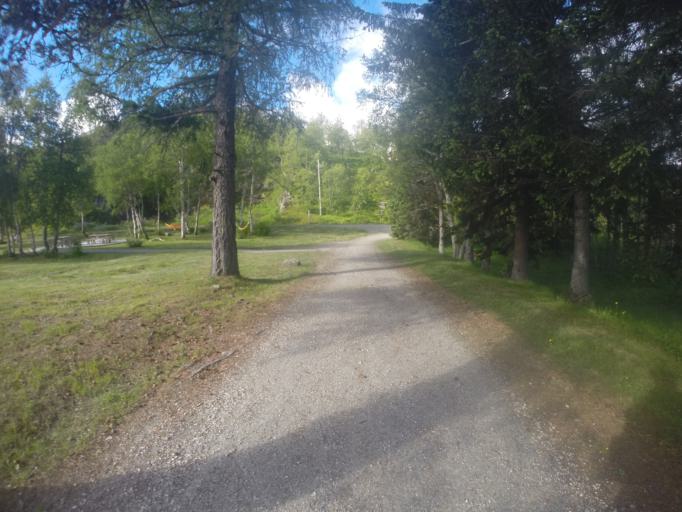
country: NO
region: Sogn og Fjordane
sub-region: Aurland
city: Aurlandsvangen
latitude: 60.7434
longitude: 7.1303
